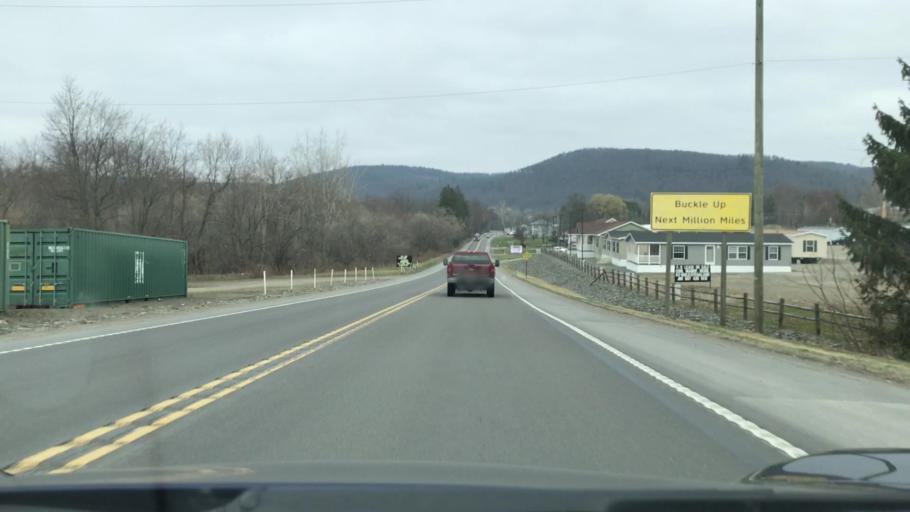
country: US
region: Pennsylvania
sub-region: Bradford County
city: Towanda
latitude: 41.7743
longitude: -76.3738
